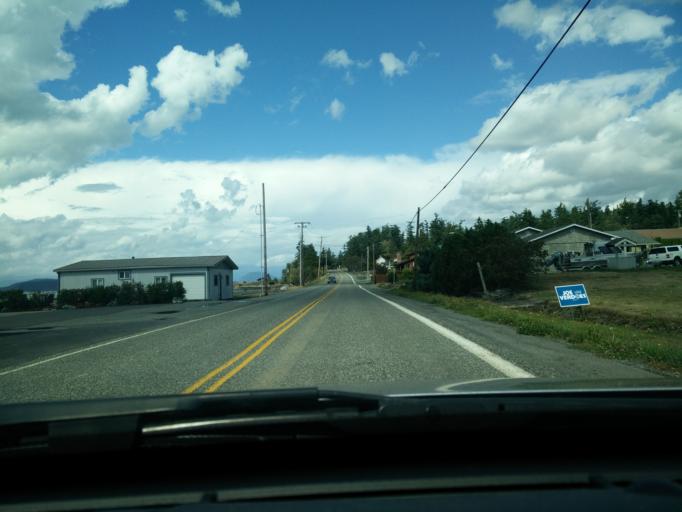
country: US
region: Washington
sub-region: Skagit County
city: Anacortes
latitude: 48.4843
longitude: -122.4782
